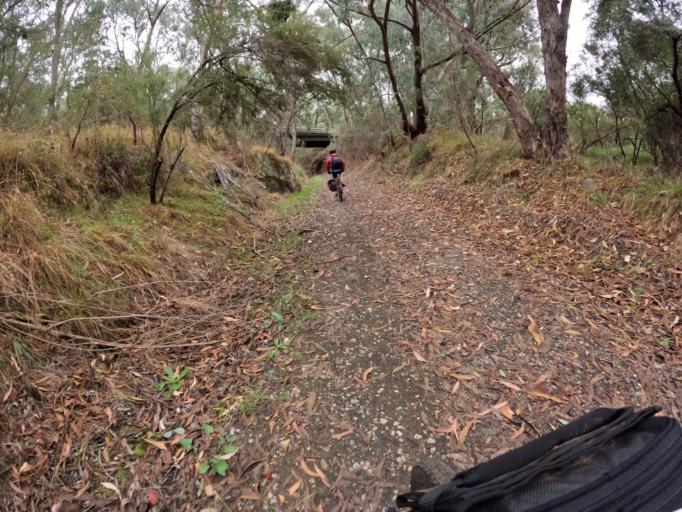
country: AU
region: New South Wales
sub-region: Greater Hume Shire
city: Holbrook
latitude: -36.1668
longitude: 147.4054
